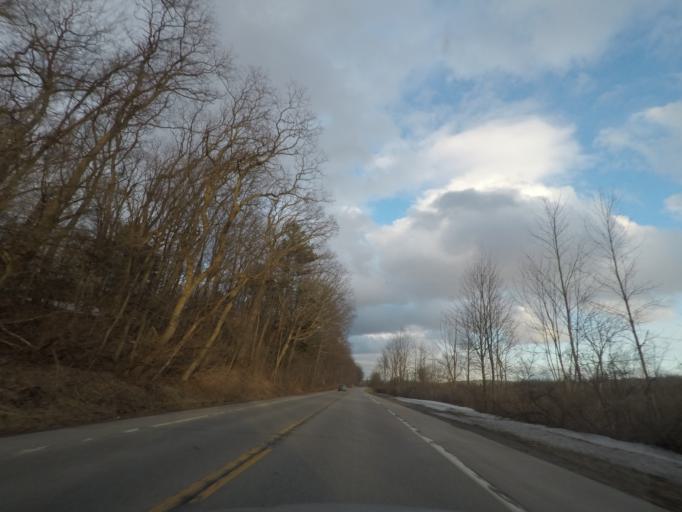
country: US
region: New York
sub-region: Montgomery County
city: Saint Johnsville
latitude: 43.0078
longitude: -74.7568
